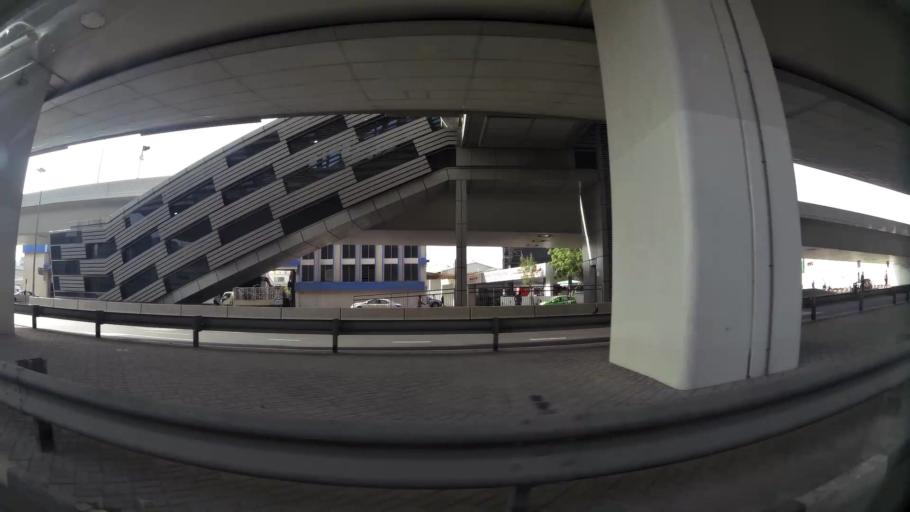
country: AE
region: Ash Shariqah
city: Sharjah
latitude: 25.2755
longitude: 55.3466
